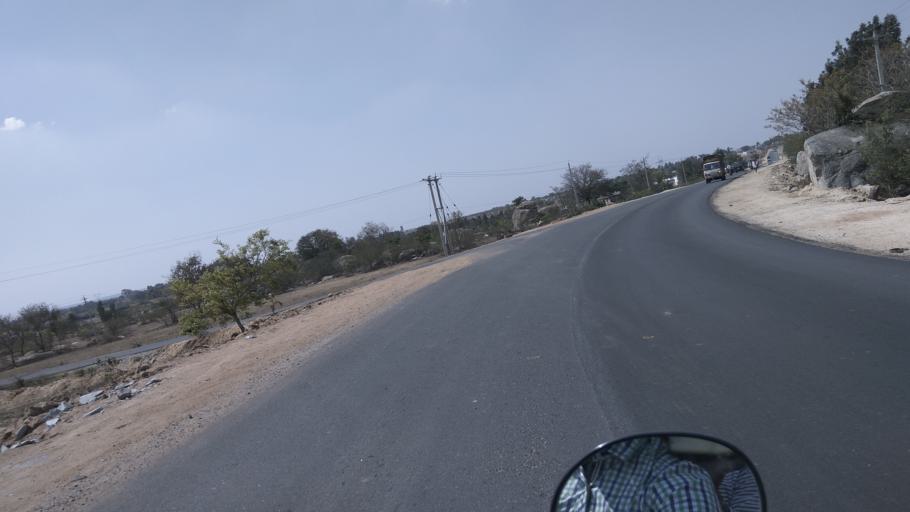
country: IN
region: Karnataka
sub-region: Kolar
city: Mulbagal
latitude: 13.1755
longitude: 78.3542
